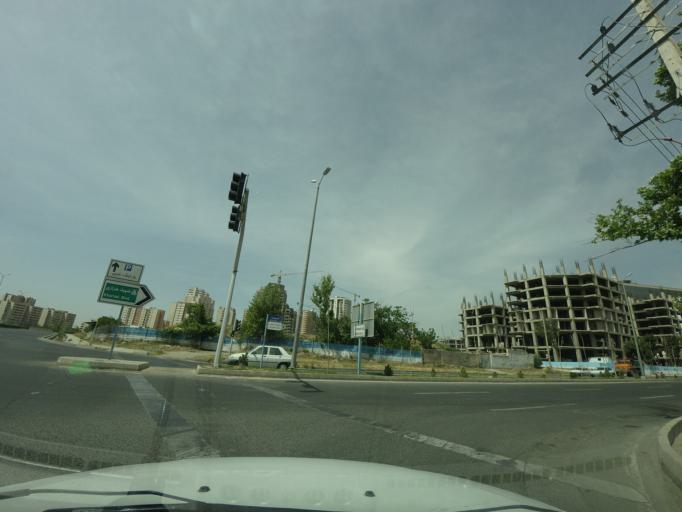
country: IR
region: Tehran
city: Shahr-e Qods
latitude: 35.7506
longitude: 51.1999
